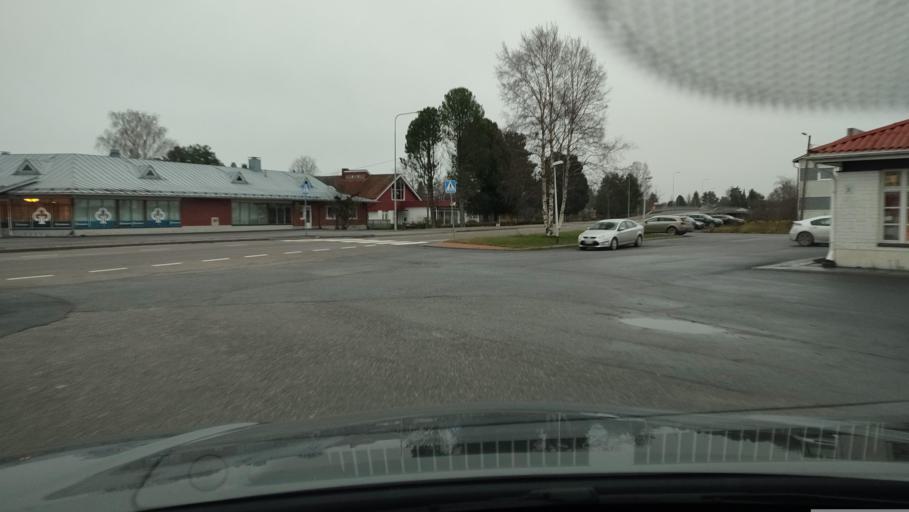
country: FI
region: Ostrobothnia
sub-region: Sydosterbotten
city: Kristinestad
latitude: 62.2545
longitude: 21.5077
